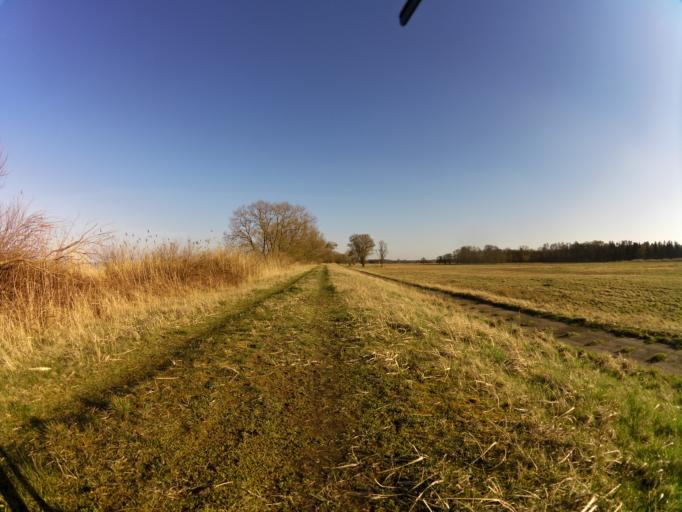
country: PL
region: West Pomeranian Voivodeship
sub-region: Powiat policki
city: Nowe Warpno
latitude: 53.7115
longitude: 14.3484
